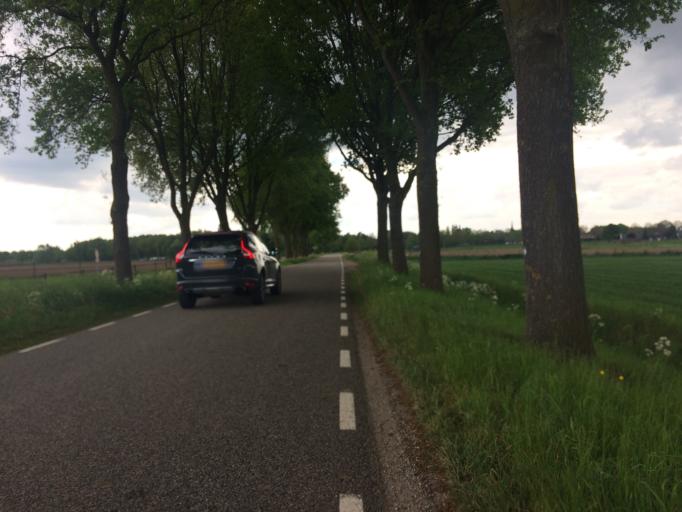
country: NL
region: Gelderland
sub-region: Gemeente Maasdriel
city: Hedel
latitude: 51.7090
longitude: 5.2381
